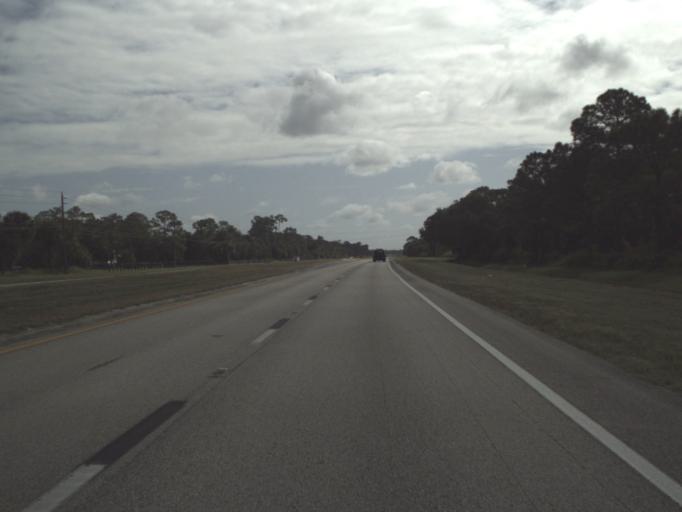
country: US
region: Florida
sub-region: Lee County
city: Alva
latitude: 26.7128
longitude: -81.6545
